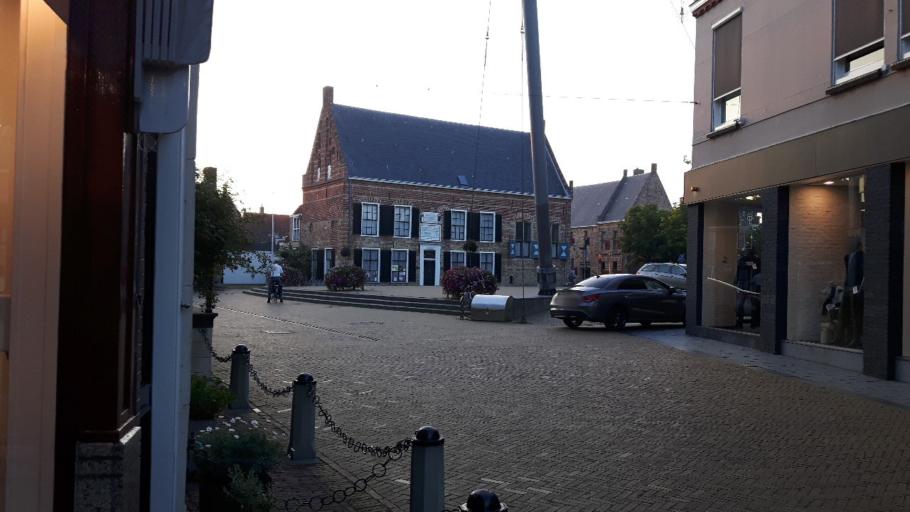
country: NL
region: Friesland
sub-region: Gemeente Franekeradeel
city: Franeker
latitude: 53.1859
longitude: 5.5447
